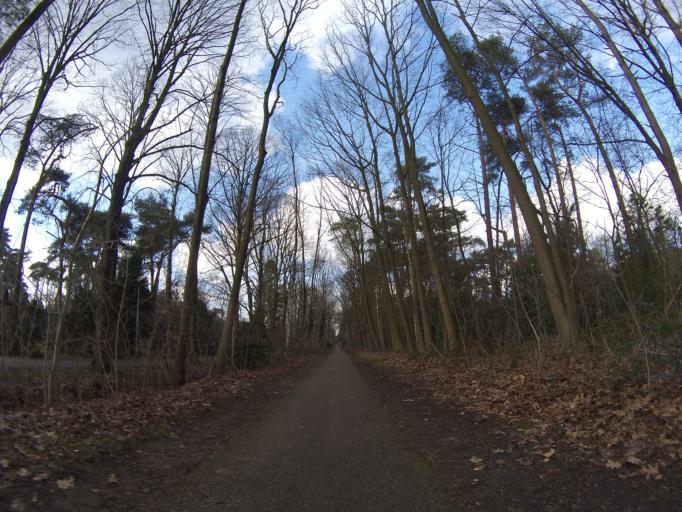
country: NL
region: Utrecht
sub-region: Gemeente Zeist
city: Zeist
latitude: 52.1188
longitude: 5.2416
